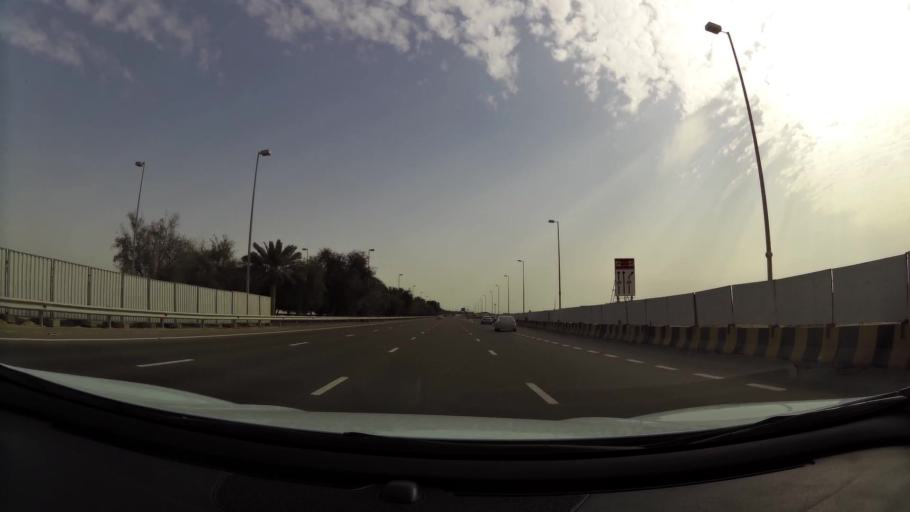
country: AE
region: Abu Dhabi
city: Abu Dhabi
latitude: 24.4295
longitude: 54.6776
